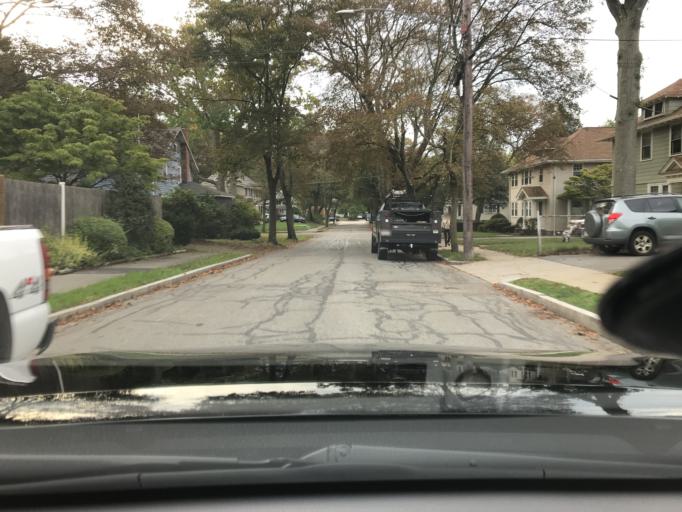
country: US
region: Massachusetts
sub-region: Middlesex County
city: Newton
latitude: 42.3526
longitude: -71.2223
